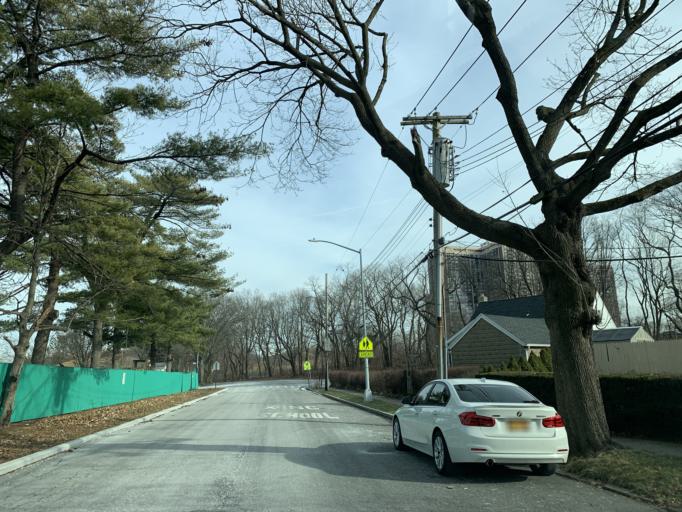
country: US
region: New York
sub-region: Nassau County
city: Lake Success
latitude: 40.7587
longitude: -73.7211
